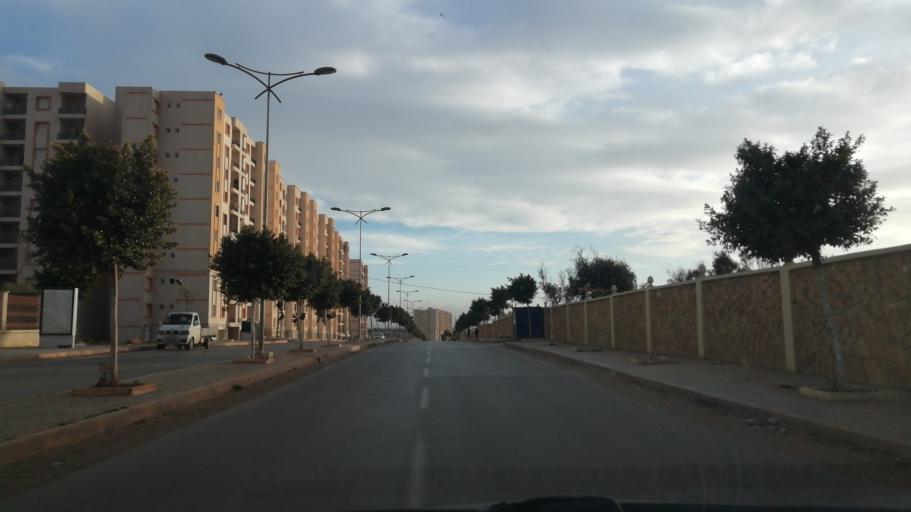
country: DZ
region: Oran
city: Bir el Djir
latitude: 35.6932
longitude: -0.5858
